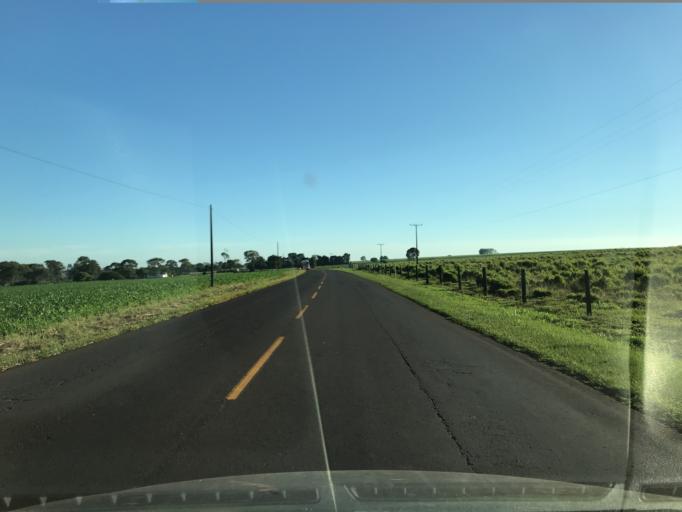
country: BR
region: Parana
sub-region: Ipora
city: Ipora
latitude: -24.1014
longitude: -53.8386
